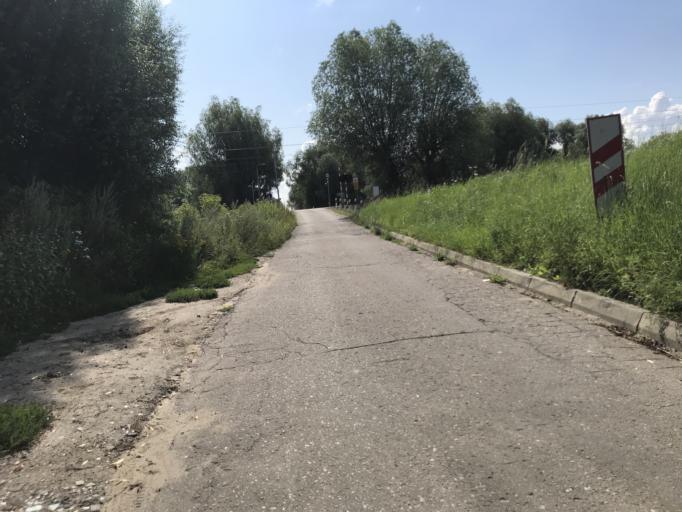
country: PL
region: Pomeranian Voivodeship
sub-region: Gdansk
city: Gdansk
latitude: 54.3259
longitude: 18.6580
